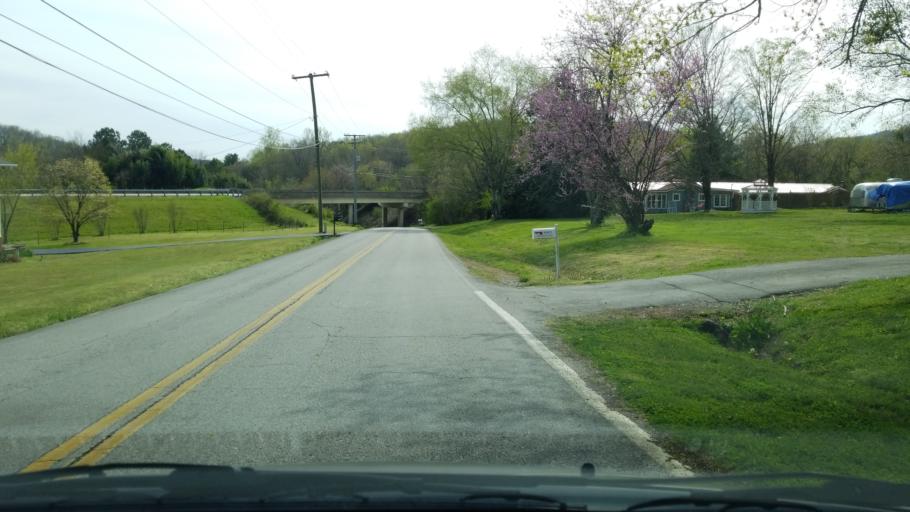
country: US
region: Tennessee
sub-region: Hamilton County
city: Falling Water
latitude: 35.1863
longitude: -85.2534
